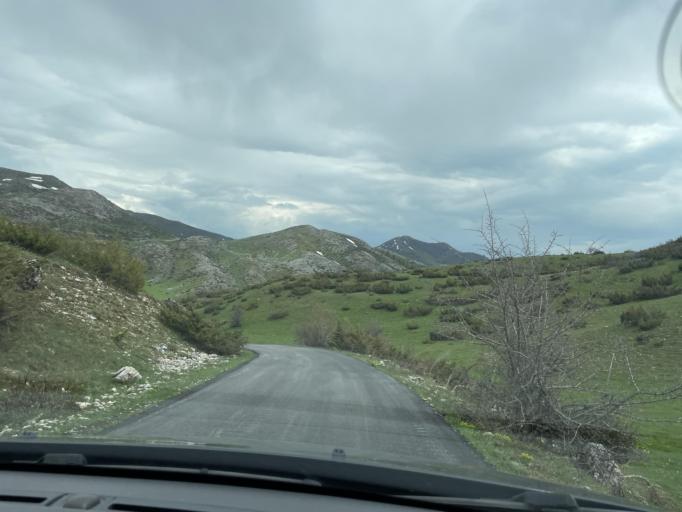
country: MK
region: Opstina Rostusa
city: Rostusha
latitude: 41.6257
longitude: 20.6807
